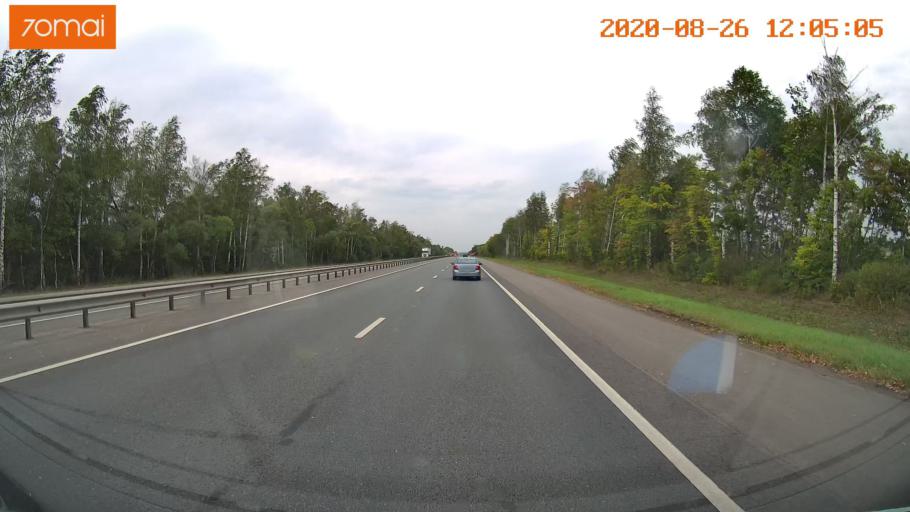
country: RU
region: Rjazan
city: Kiritsy
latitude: 54.3170
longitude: 40.1757
